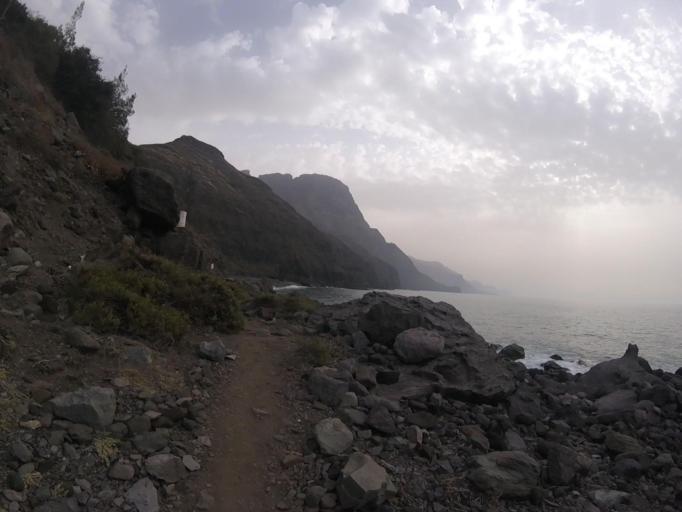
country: ES
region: Canary Islands
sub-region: Provincia de Las Palmas
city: Agaete
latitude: 28.0857
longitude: -15.7101
